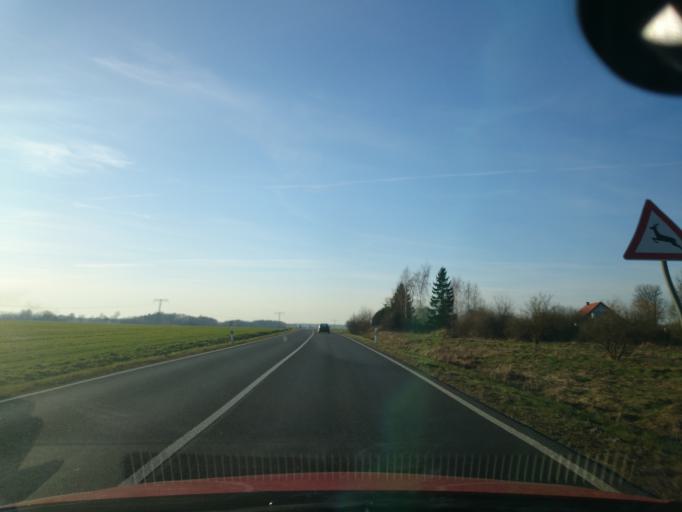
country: DE
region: Mecklenburg-Vorpommern
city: Mesekenhagen
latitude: 54.1420
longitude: 13.3280
